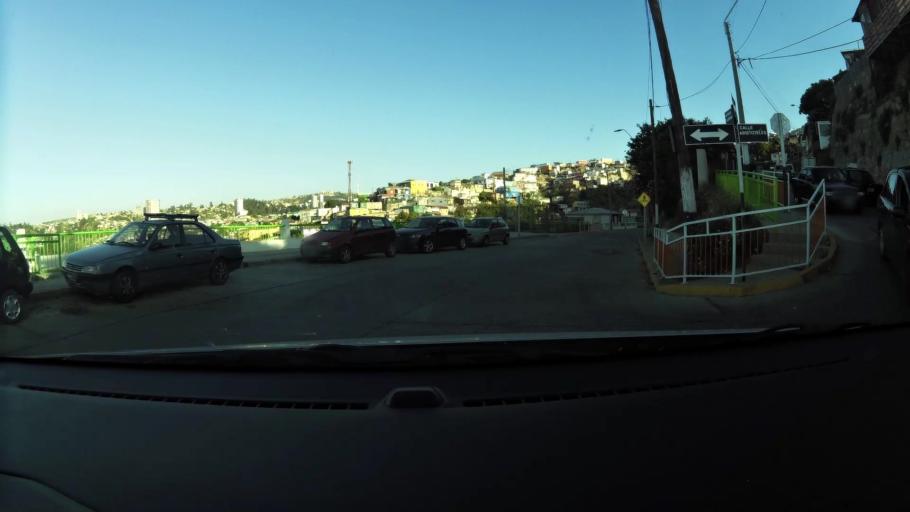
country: CL
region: Valparaiso
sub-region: Provincia de Valparaiso
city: Valparaiso
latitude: -33.0557
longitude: -71.6077
